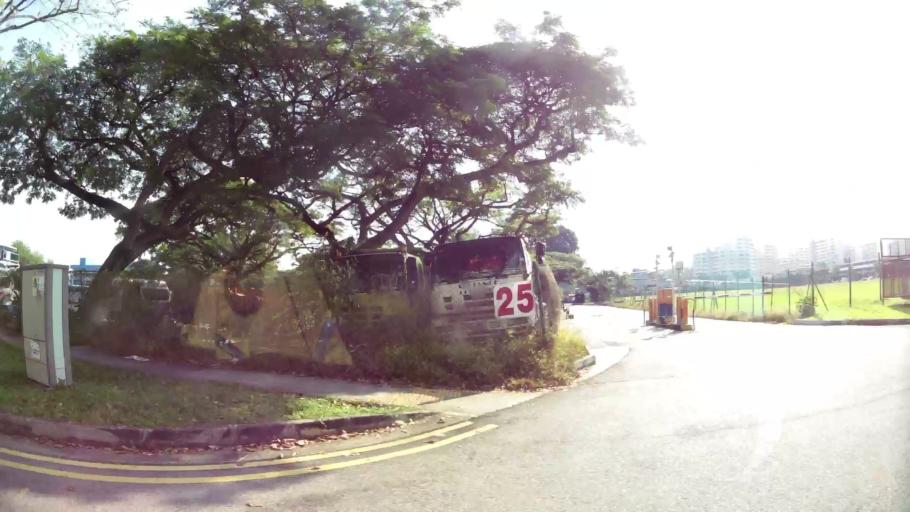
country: SG
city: Singapore
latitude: 1.3386
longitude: 103.8599
